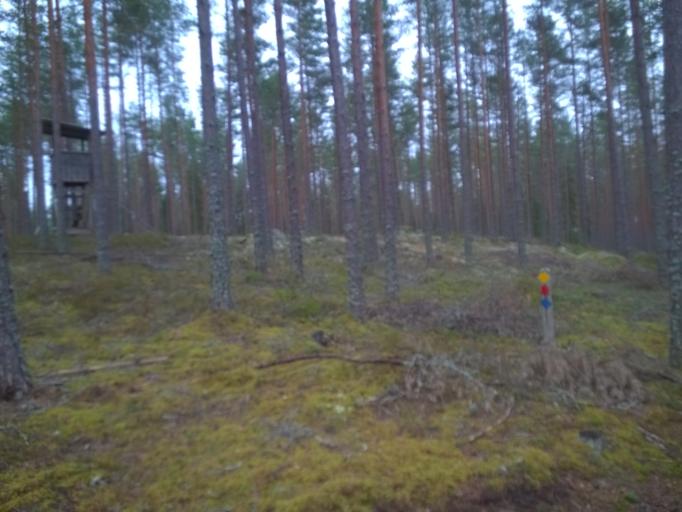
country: SE
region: Uppsala
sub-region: Osthammars Kommun
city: Bjorklinge
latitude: 60.1579
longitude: 17.5002
